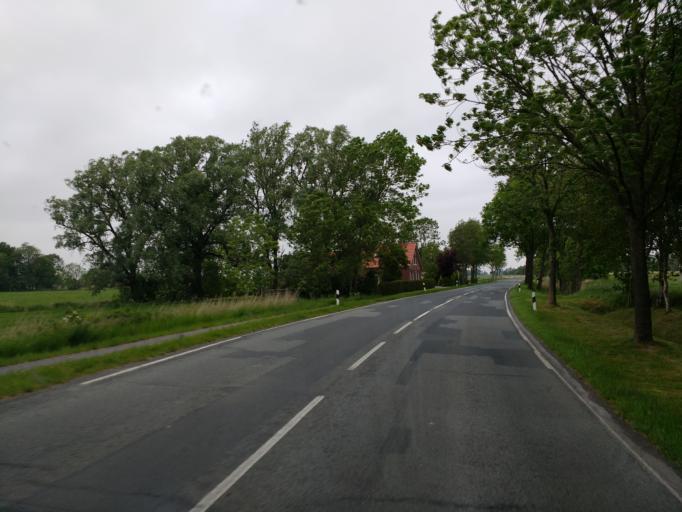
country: DE
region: Lower Saxony
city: Jever
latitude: 53.6287
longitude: 7.9246
